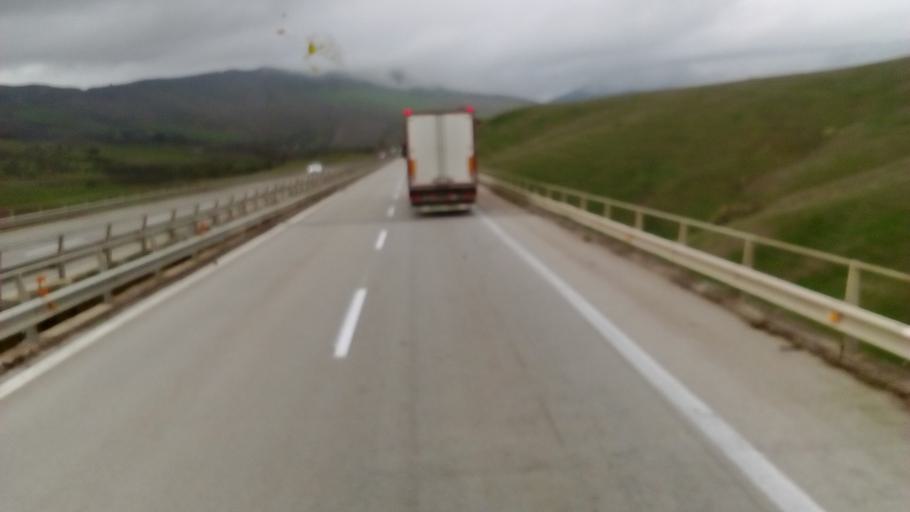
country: IT
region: Sicily
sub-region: Enna
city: Calascibetta
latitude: 37.5745
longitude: 14.2352
